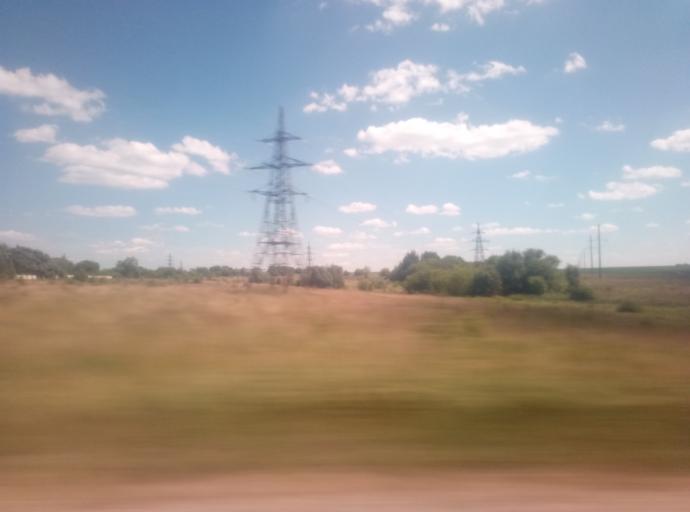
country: RU
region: Tula
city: Kireyevsk
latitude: 53.9519
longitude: 37.9391
